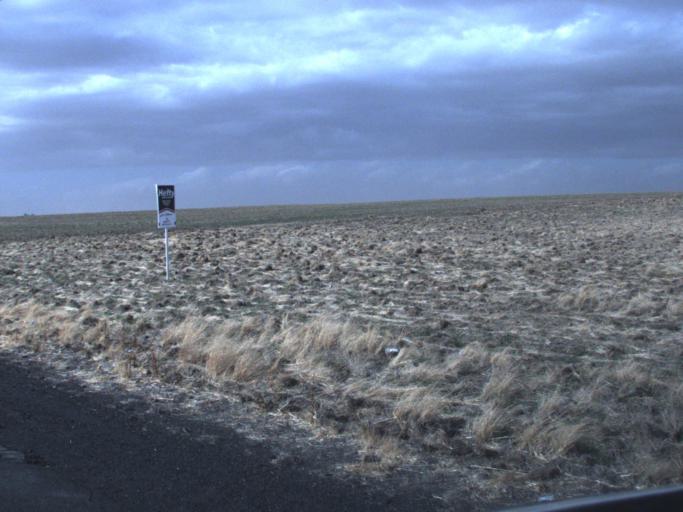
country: US
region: Washington
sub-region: Okanogan County
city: Coulee Dam
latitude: 47.6123
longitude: -118.7742
